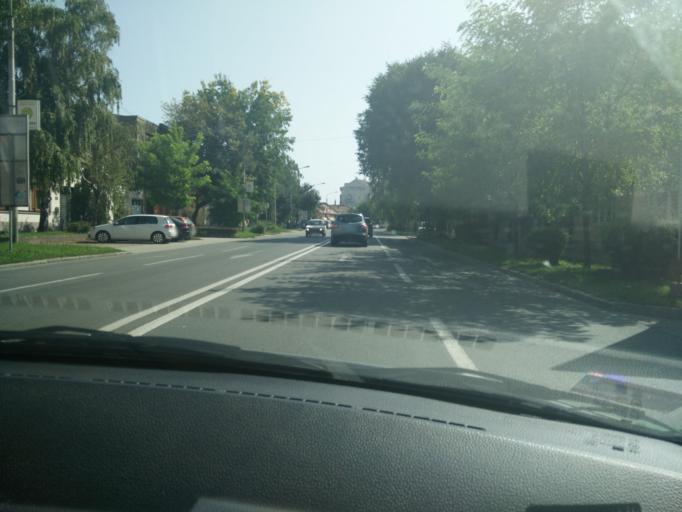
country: RS
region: Autonomna Pokrajina Vojvodina
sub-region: Juznobacki Okrug
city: Novi Sad
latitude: 45.2669
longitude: 19.8433
